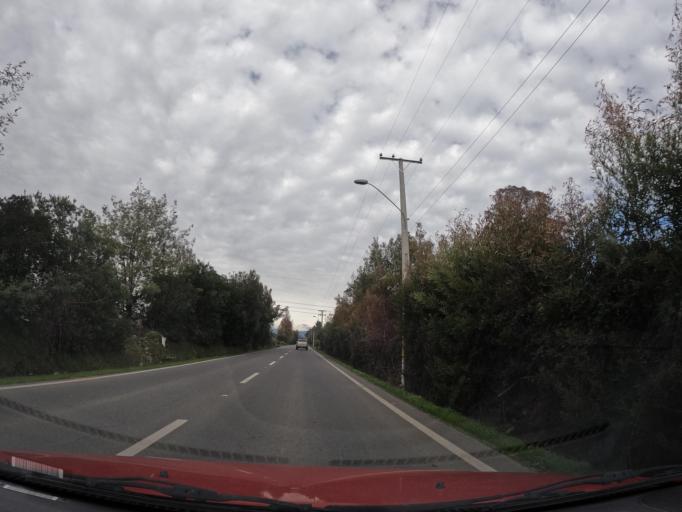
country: CL
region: Maule
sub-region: Provincia de Linares
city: Linares
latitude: -35.8897
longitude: -71.5278
